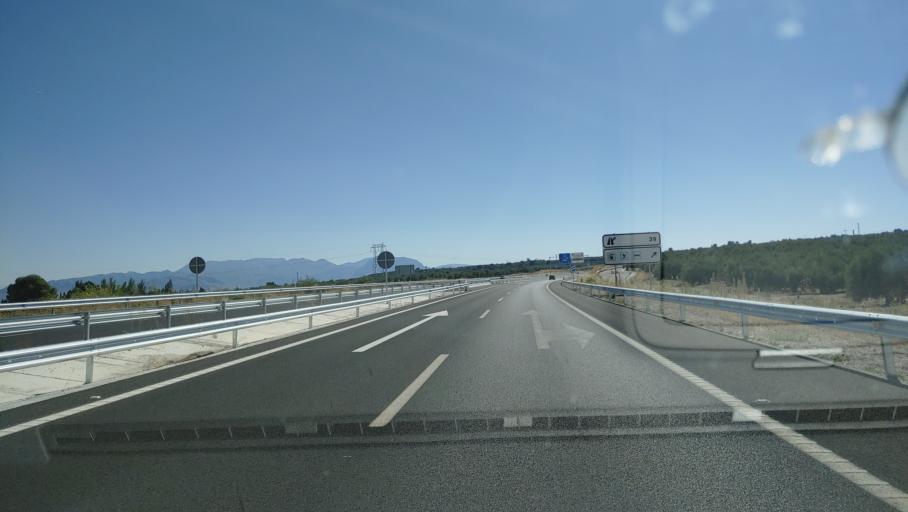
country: ES
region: Andalusia
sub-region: Provincia de Jaen
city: Sabiote
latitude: 38.0372
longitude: -3.3249
